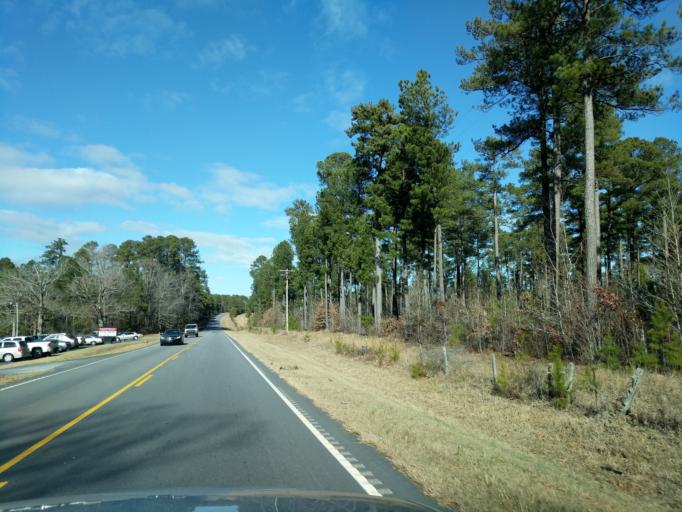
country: US
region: South Carolina
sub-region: Edgefield County
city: Edgefield
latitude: 33.9393
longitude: -82.0481
